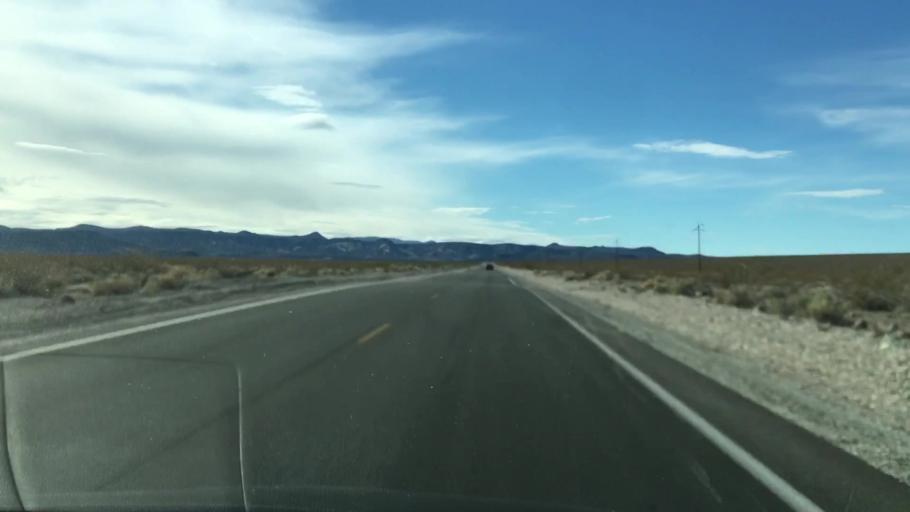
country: US
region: Nevada
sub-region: Nye County
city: Pahrump
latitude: 36.3033
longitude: -116.4822
